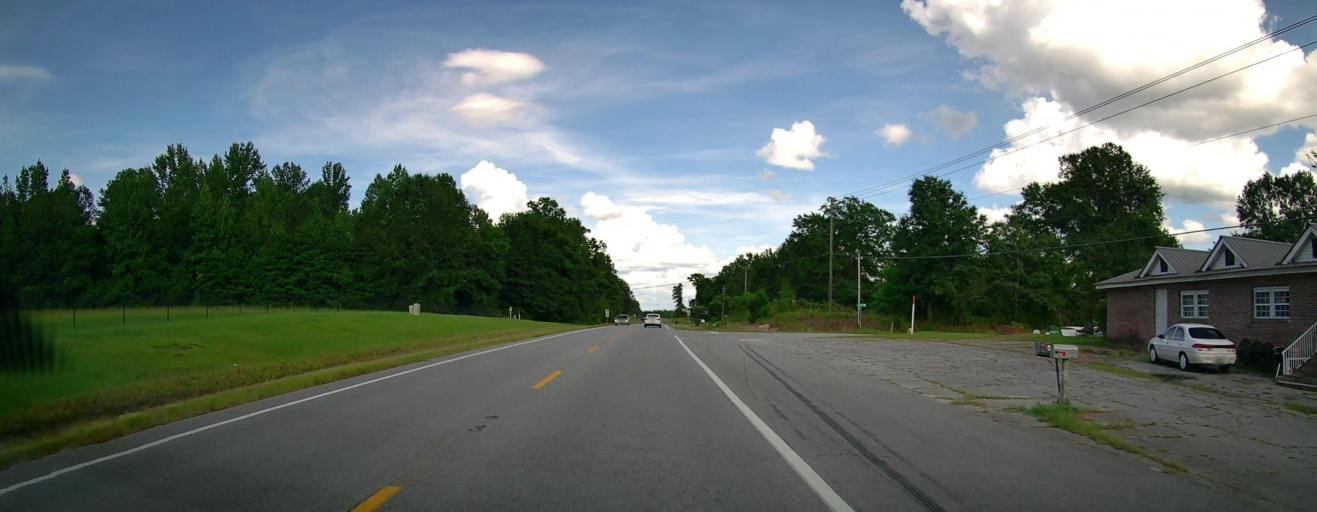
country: US
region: Alabama
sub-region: Russell County
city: Ladonia
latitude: 32.4621
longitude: -85.1676
